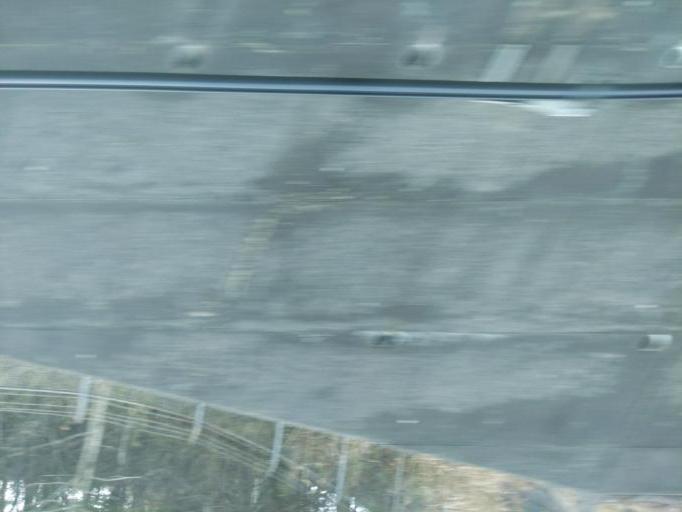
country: JP
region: Miyagi
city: Kogota
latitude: 38.7329
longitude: 141.0627
